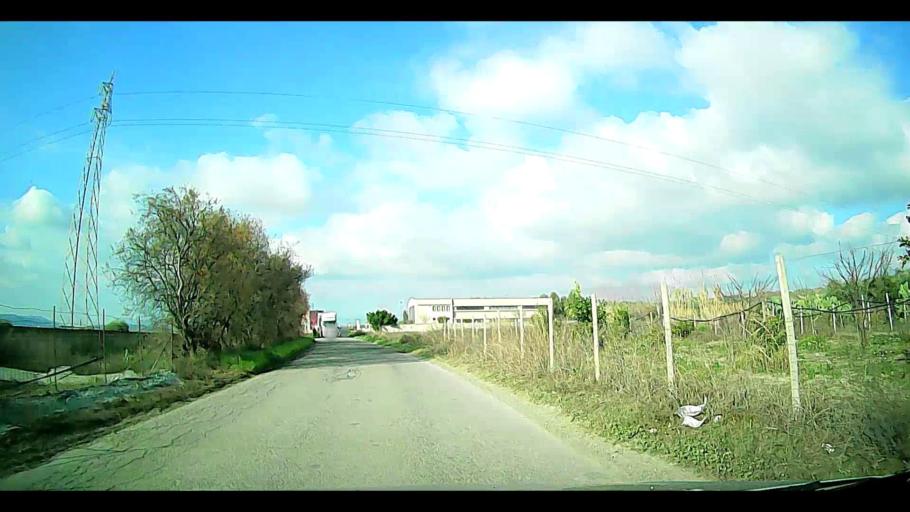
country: IT
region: Calabria
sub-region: Provincia di Crotone
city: Rocca di Neto
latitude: 39.1822
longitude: 17.0446
